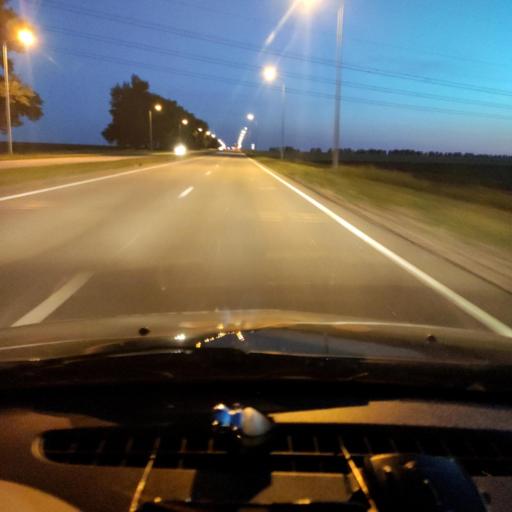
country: RU
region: Belgorod
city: Skorodnoye
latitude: 51.1767
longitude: 37.3355
